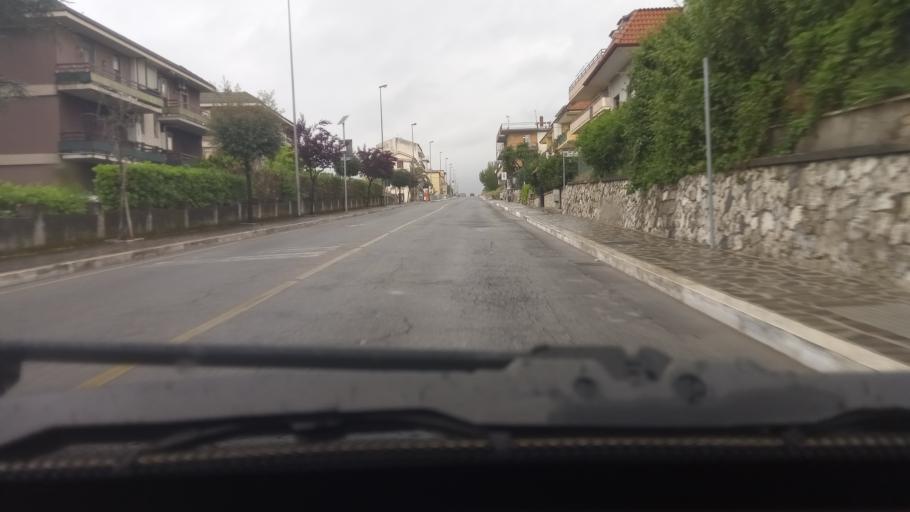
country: IT
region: Latium
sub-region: Provincia di Latina
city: Penitro
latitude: 41.2587
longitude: 13.6989
